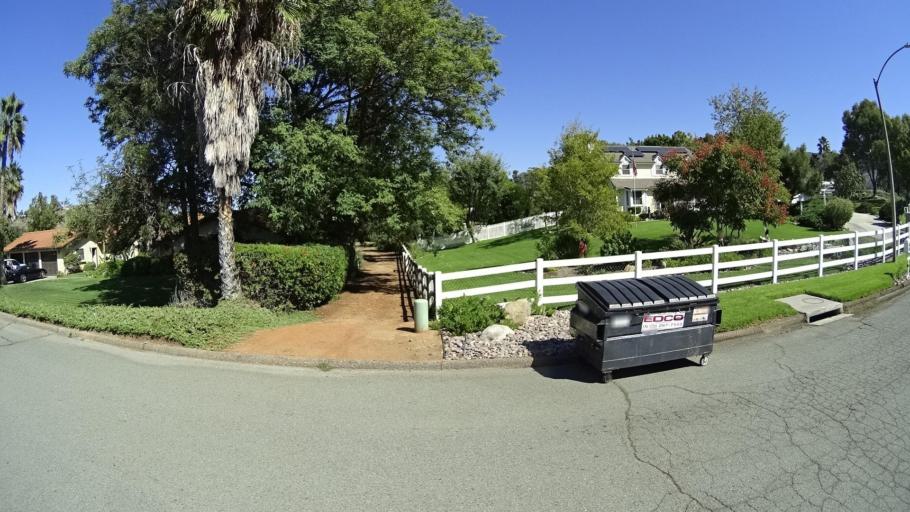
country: US
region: California
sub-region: San Diego County
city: Rancho San Diego
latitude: 32.7415
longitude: -116.9058
